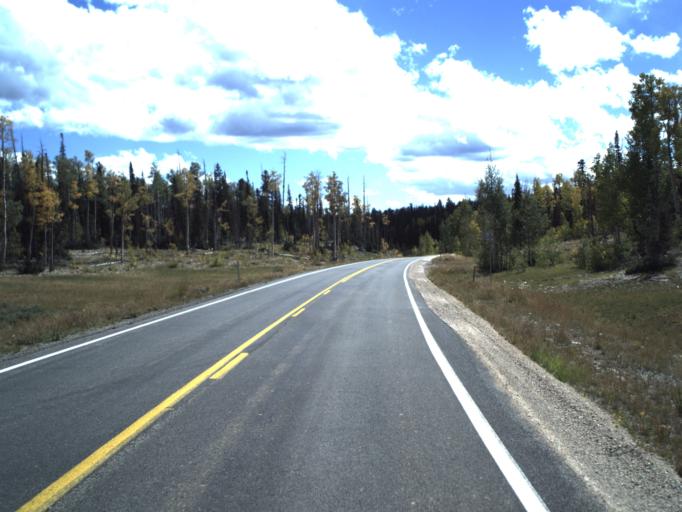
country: US
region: Utah
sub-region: Iron County
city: Parowan
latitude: 37.5488
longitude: -112.7861
